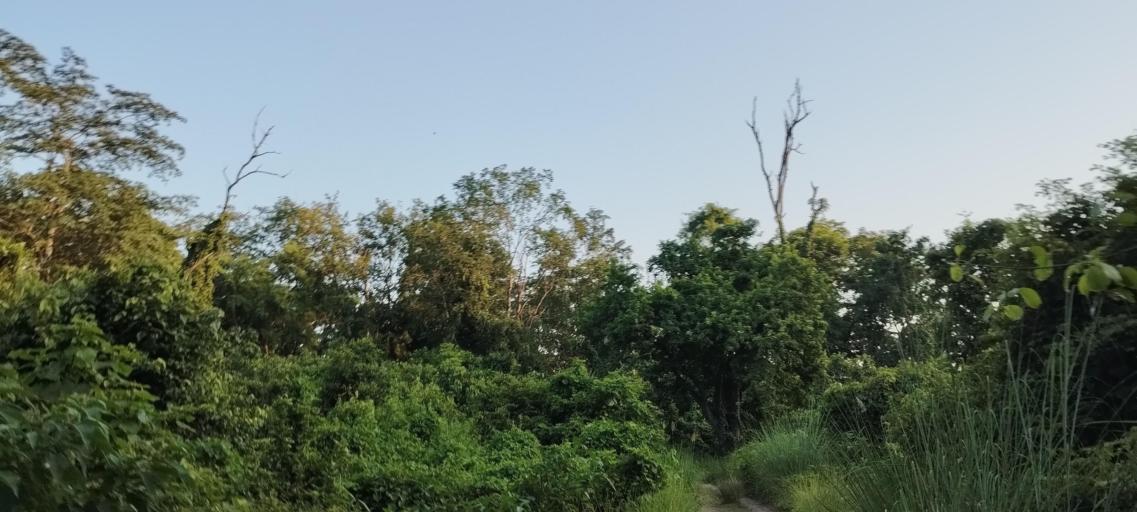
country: NP
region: Far Western
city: Tikapur
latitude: 28.4582
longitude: 81.2422
